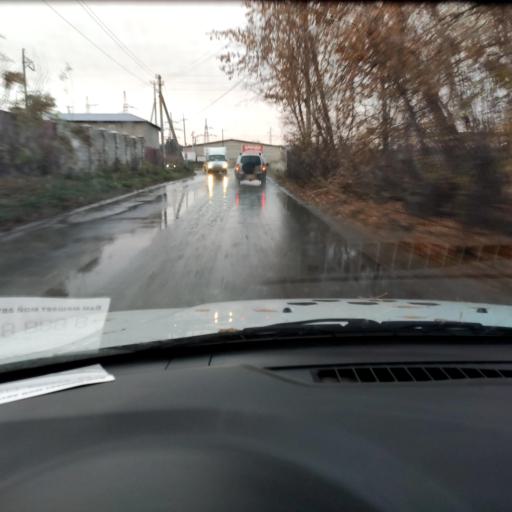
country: RU
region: Samara
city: Zhigulevsk
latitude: 53.5224
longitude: 49.4867
